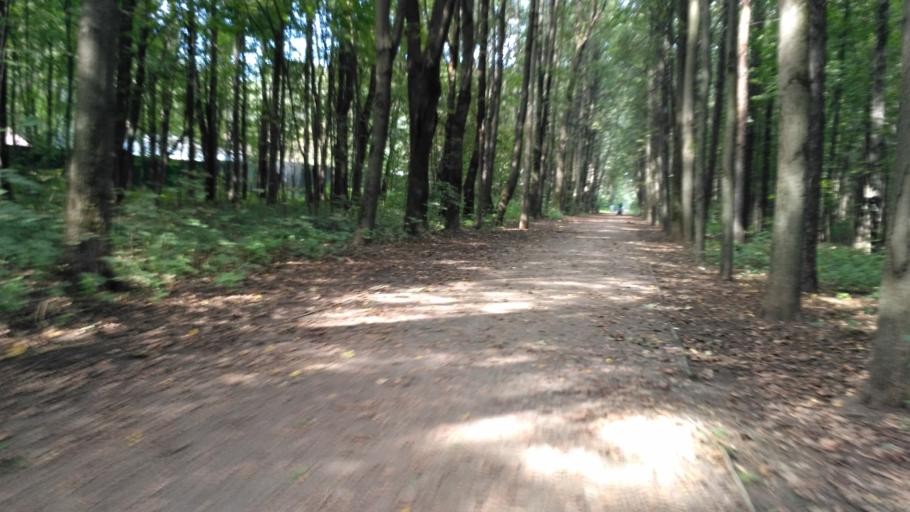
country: RU
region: Moscow
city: Ryazanskiy
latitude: 55.7682
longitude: 37.7537
